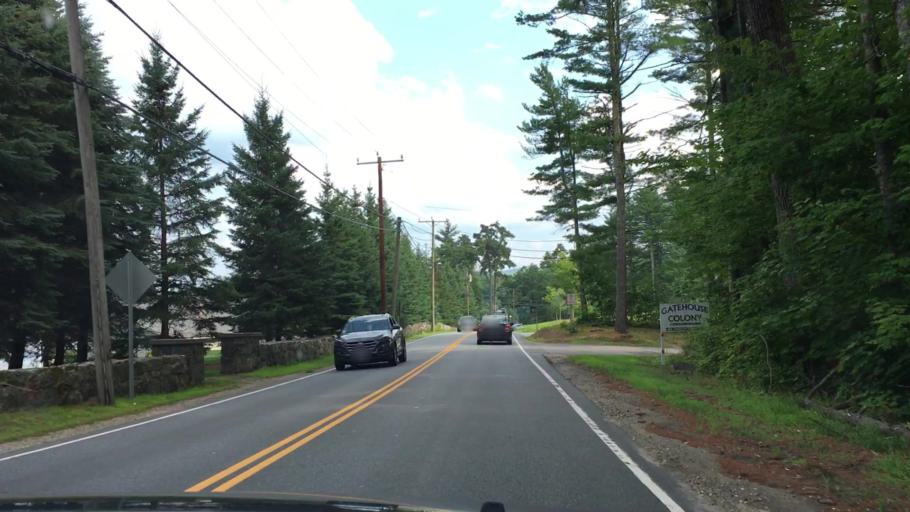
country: US
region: New Hampshire
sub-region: Belknap County
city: Gilford
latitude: 43.5993
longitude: -71.4323
